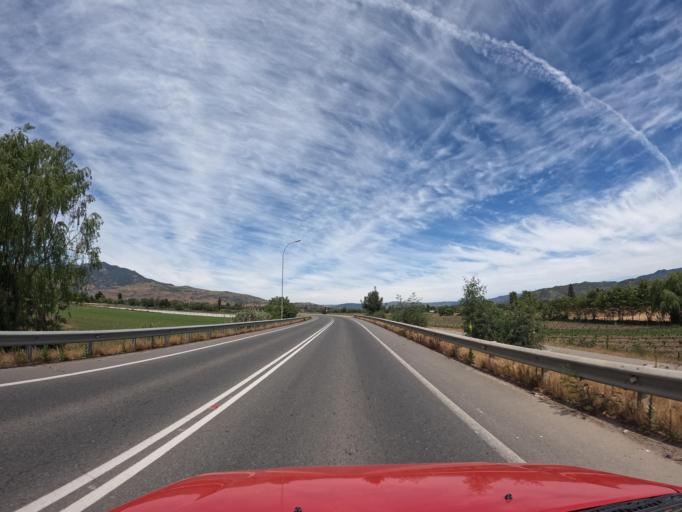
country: CL
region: Maule
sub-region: Provincia de Talca
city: Talca
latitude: -35.0950
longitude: -71.6451
